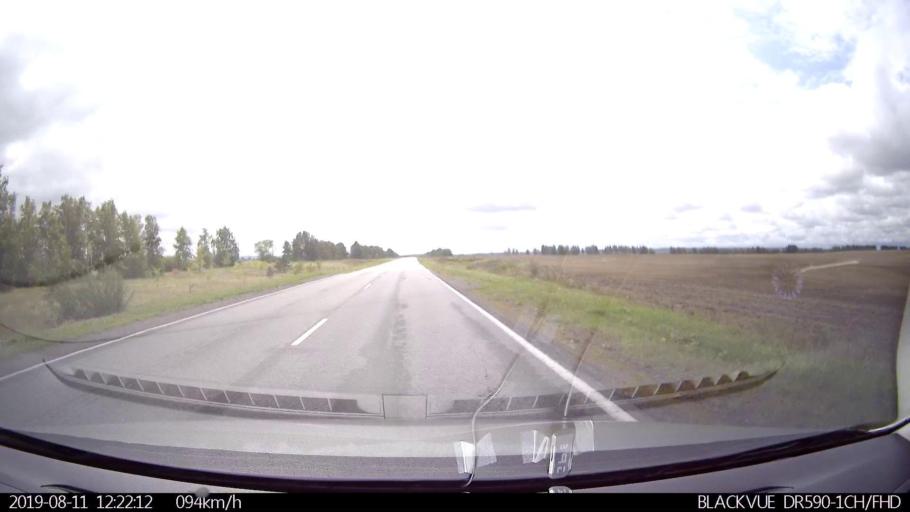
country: RU
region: Ulyanovsk
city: Ignatovka
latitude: 53.9110
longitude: 47.9550
